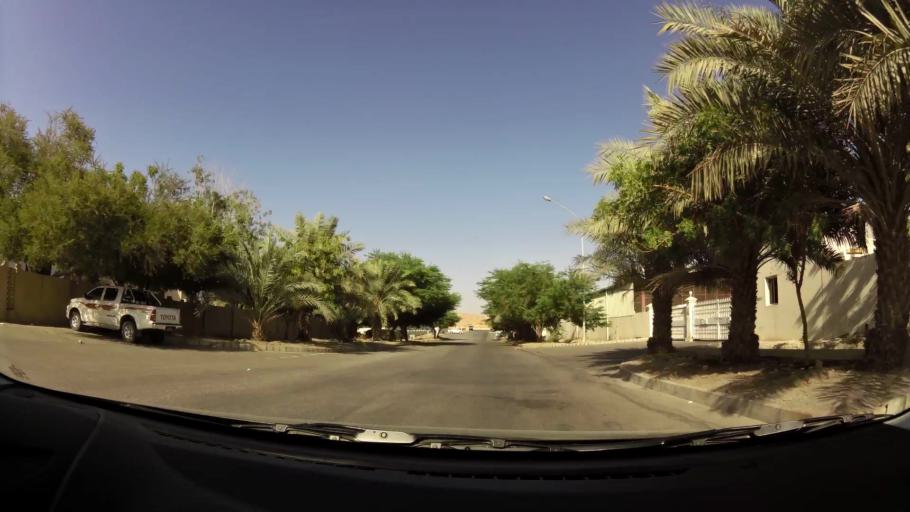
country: OM
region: Muhafazat Masqat
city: As Sib al Jadidah
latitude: 23.5520
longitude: 58.2261
